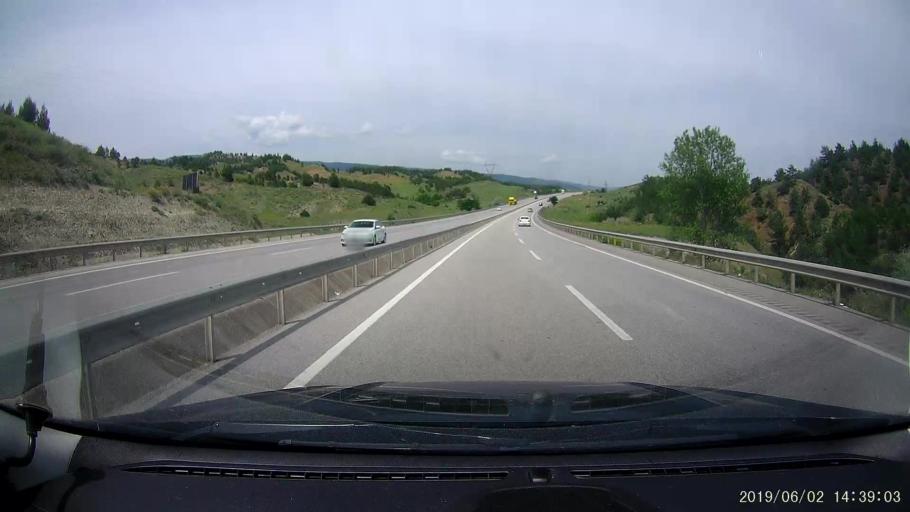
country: TR
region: Corum
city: Hacihamza
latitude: 41.0649
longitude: 34.2911
